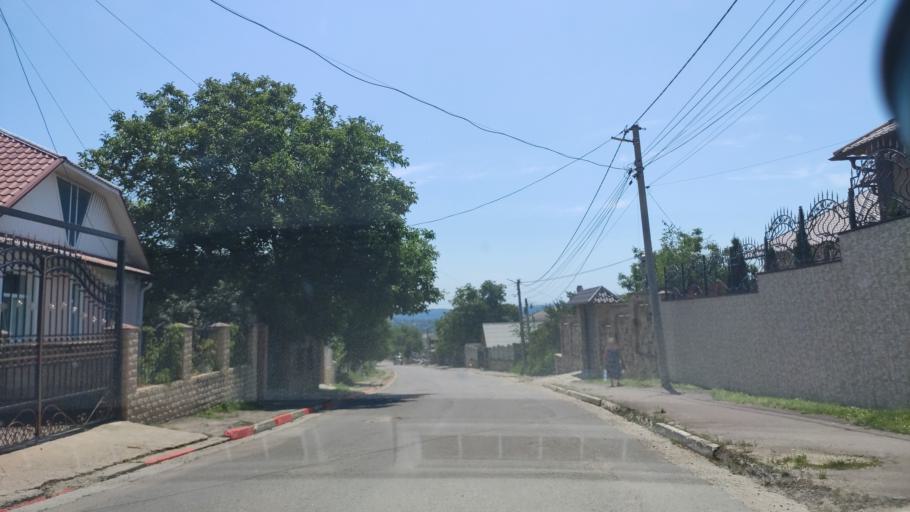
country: MD
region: Raionul Soroca
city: Soroca
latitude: 48.1693
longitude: 28.2994
